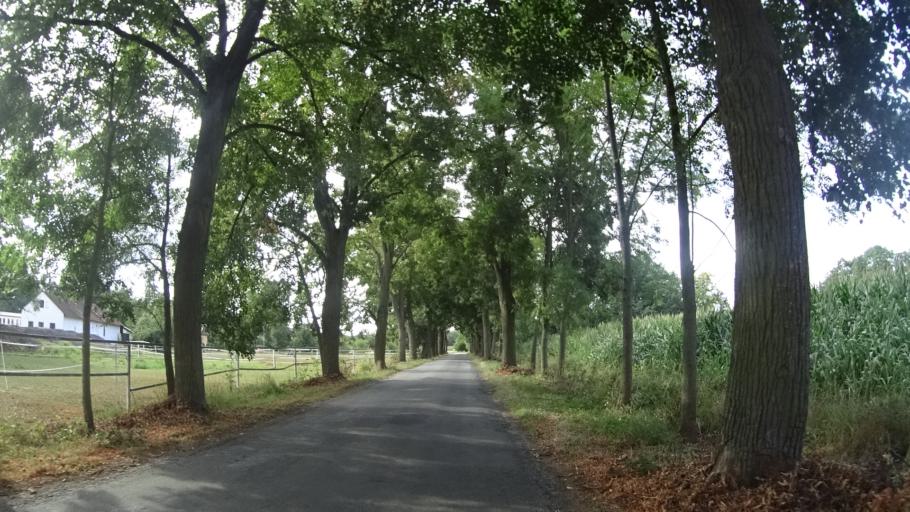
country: CZ
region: Olomoucky
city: Dubicko
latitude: 49.8038
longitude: 16.9437
